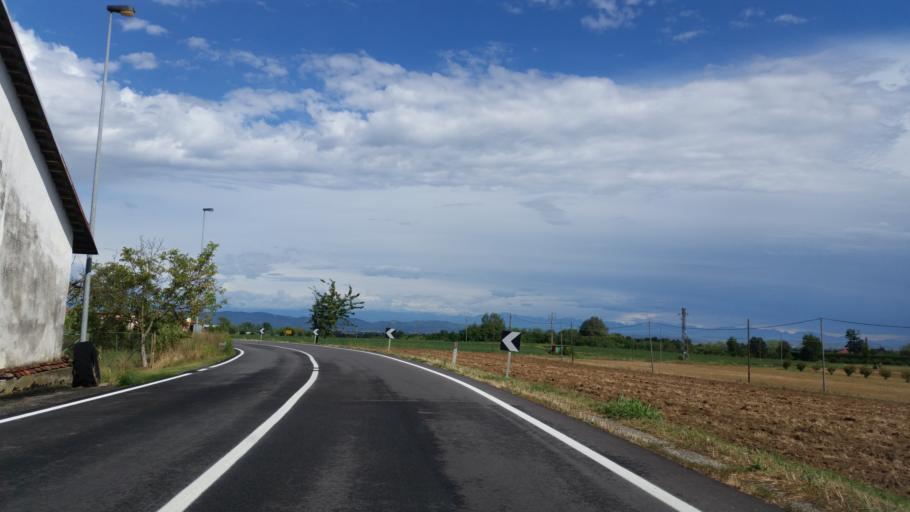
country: IT
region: Piedmont
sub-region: Provincia di Torino
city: Pralormo
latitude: 44.8701
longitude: 7.8955
